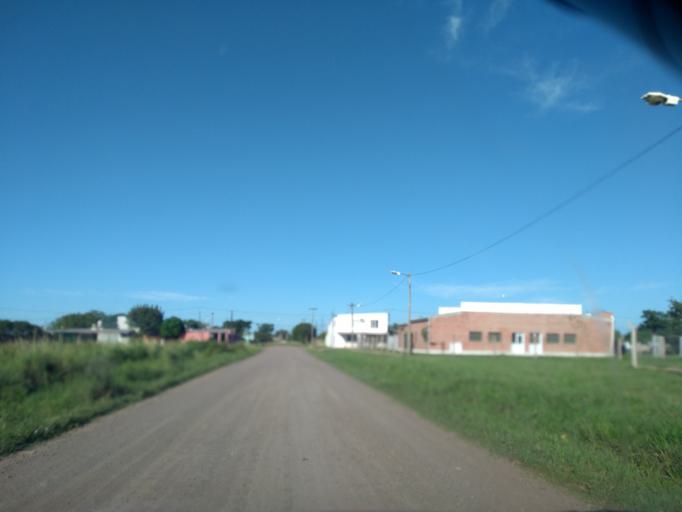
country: AR
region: Chaco
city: Fontana
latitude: -27.4195
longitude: -59.0478
